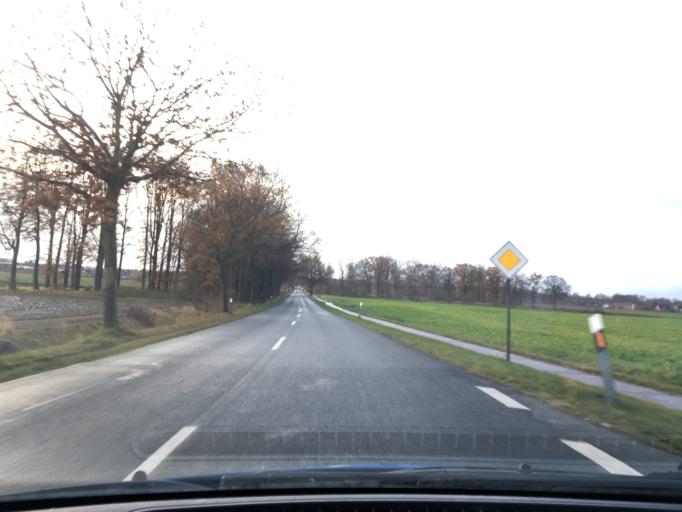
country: DE
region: Lower Saxony
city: Embsen
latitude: 53.1865
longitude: 10.3466
